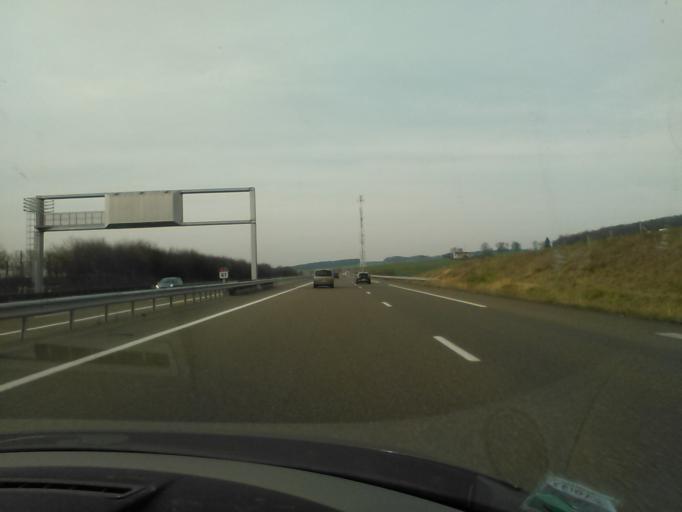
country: FR
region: Bourgogne
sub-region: Departement de l'Yonne
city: Sergines
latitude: 48.2879
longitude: 3.2676
